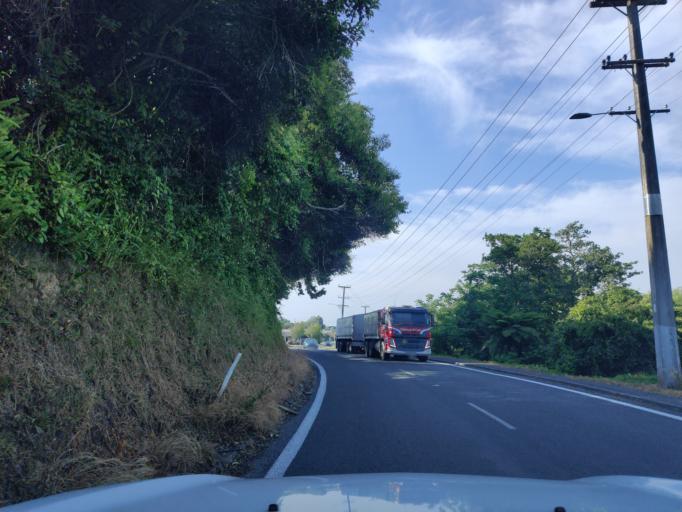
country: NZ
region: Waikato
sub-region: Waikato District
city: Ngaruawahia
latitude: -37.5758
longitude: 175.1532
